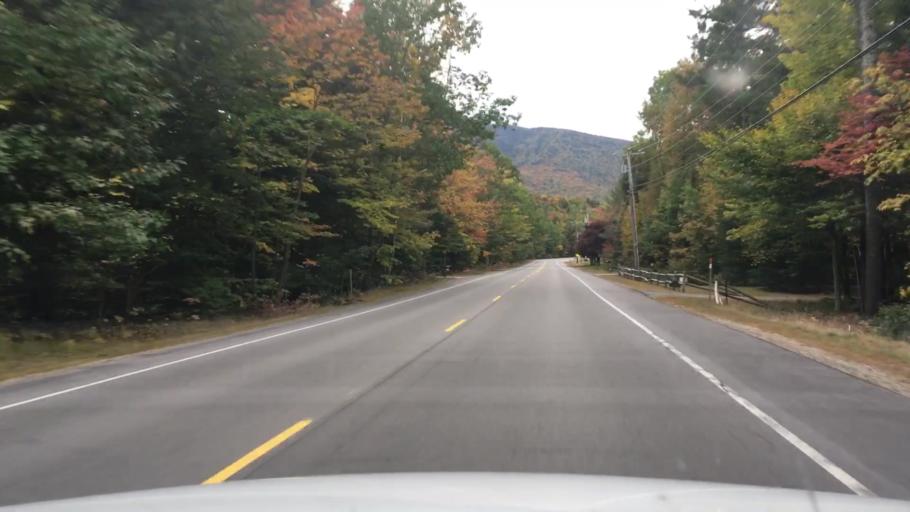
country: US
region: New Hampshire
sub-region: Coos County
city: Gorham
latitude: 44.3688
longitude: -71.1749
